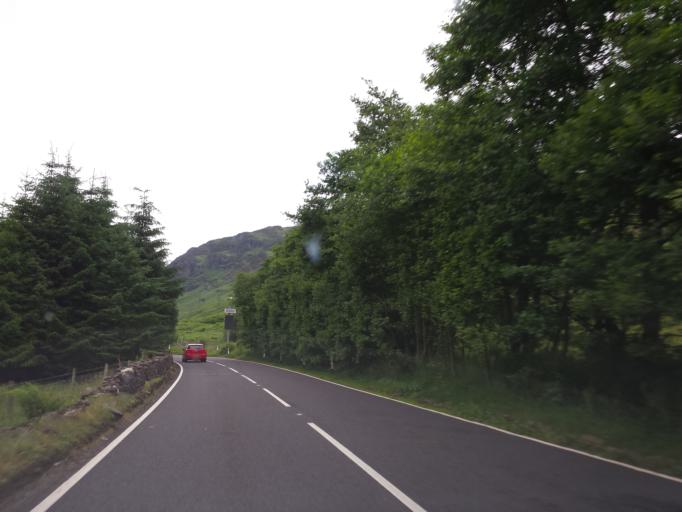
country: GB
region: Scotland
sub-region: Stirling
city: Callander
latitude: 56.3978
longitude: -4.2968
